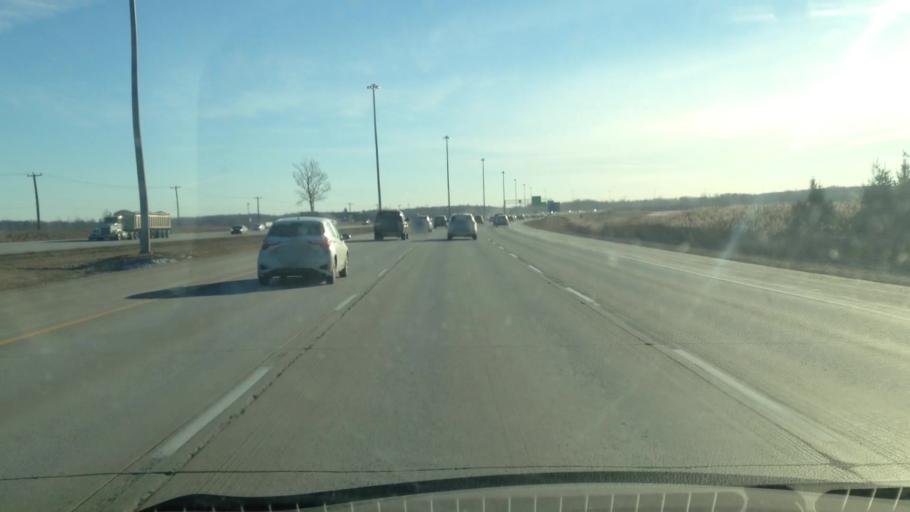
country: CA
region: Quebec
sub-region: Laurentides
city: Saint-Jerome
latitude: 45.7344
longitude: -73.9840
